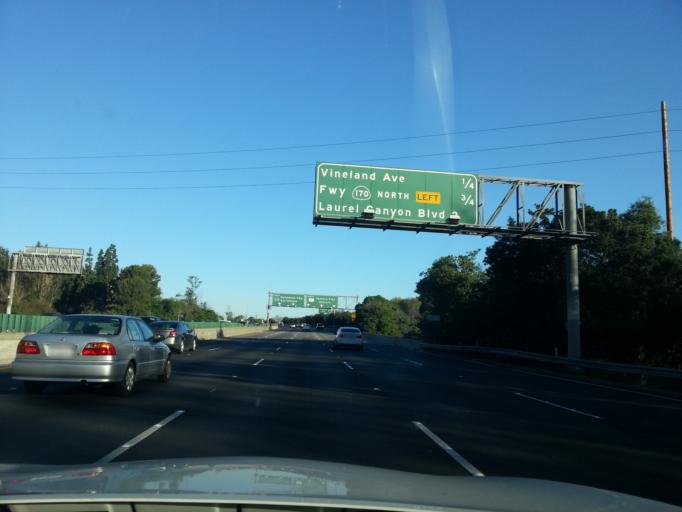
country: US
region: California
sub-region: Los Angeles County
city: Universal City
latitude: 34.1430
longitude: -118.3672
